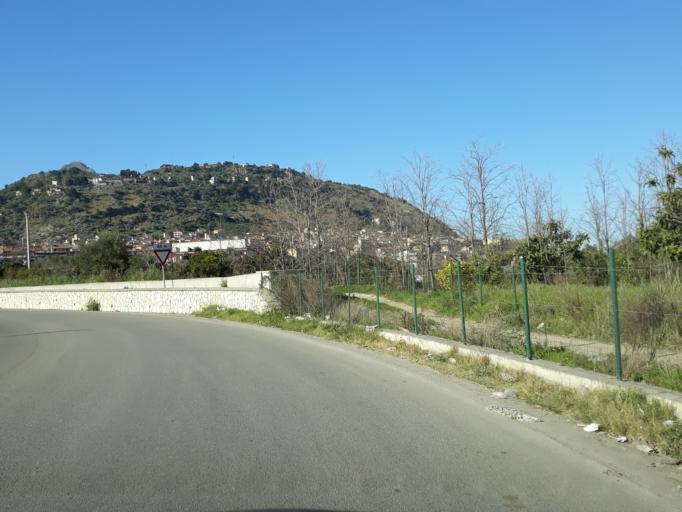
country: IT
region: Sicily
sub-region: Palermo
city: Misilmeri
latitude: 38.0279
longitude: 13.4562
